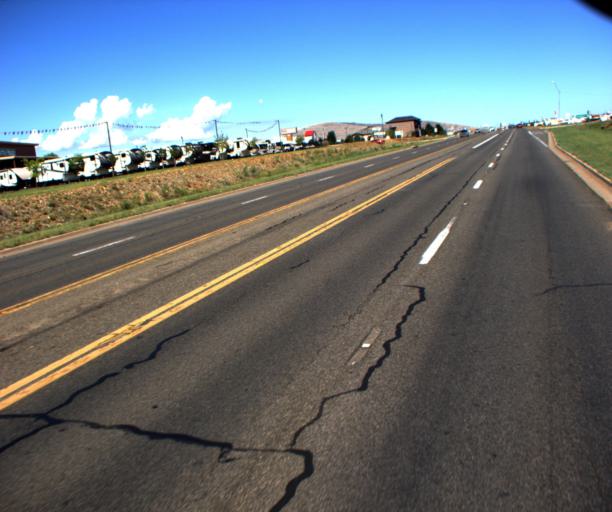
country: US
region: Arizona
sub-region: Yavapai County
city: Prescott Valley
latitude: 34.5836
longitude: -112.3101
